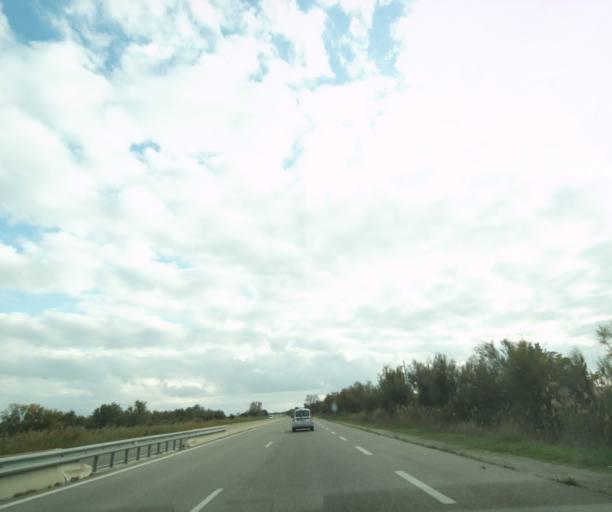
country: FR
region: Languedoc-Roussillon
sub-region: Departement du Gard
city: Aigues-Mortes
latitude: 43.6022
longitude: 4.1943
